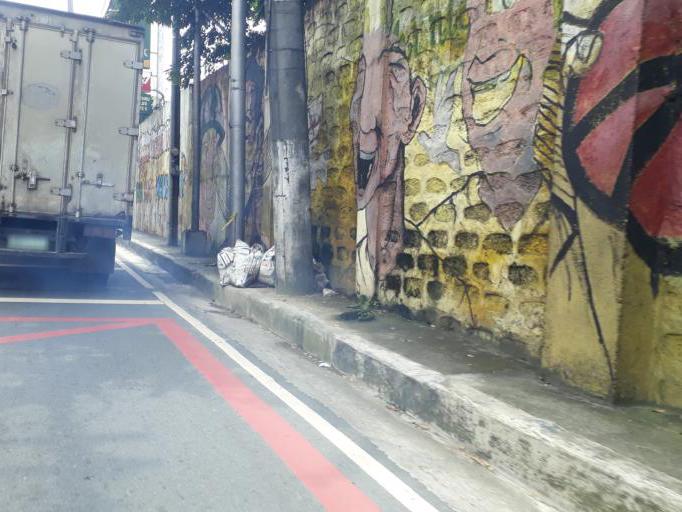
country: PH
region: Metro Manila
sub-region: Pasig
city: Pasig City
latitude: 14.6123
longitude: 121.0610
